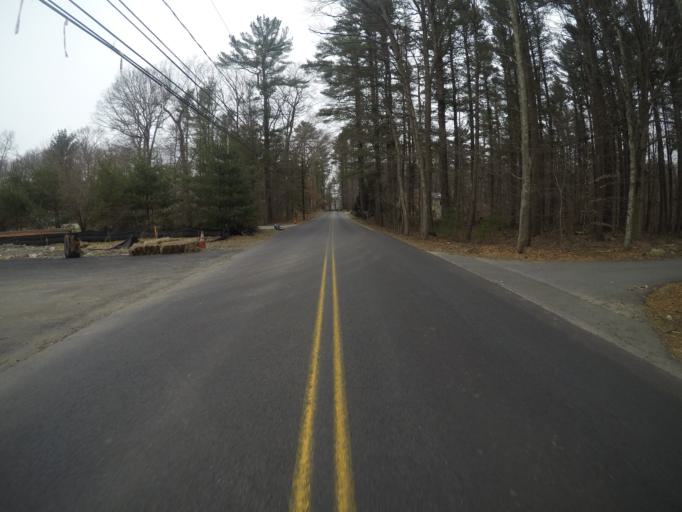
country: US
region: Massachusetts
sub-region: Bristol County
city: Easton
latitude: 42.0426
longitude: -71.1598
